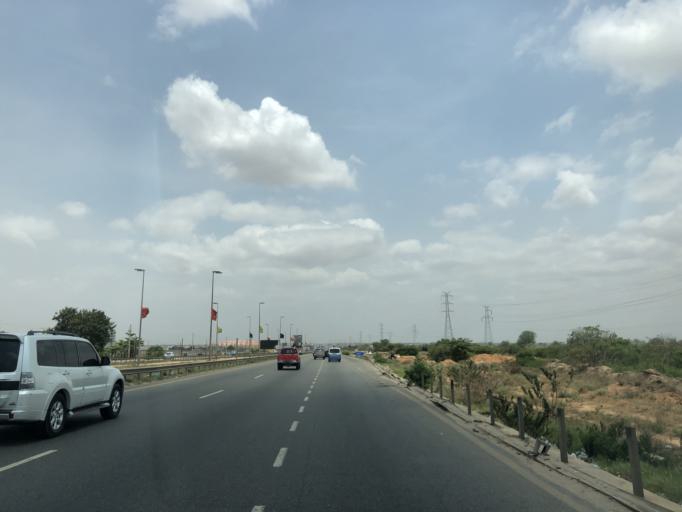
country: AO
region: Luanda
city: Luanda
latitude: -8.9736
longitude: 13.2590
